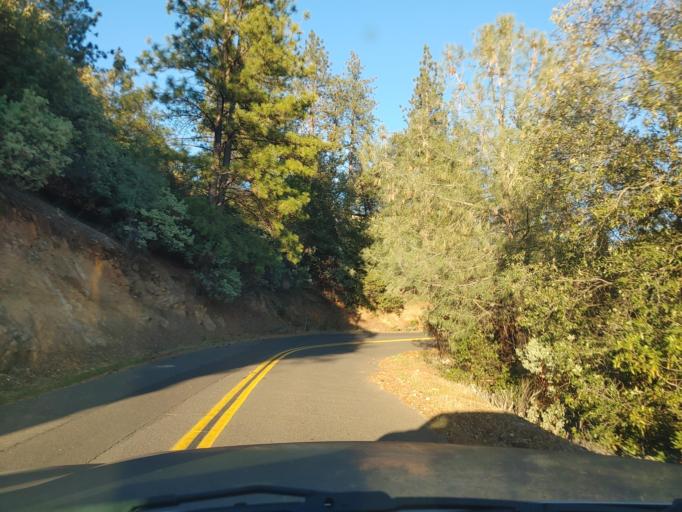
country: US
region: California
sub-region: Tuolumne County
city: Columbia
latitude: 38.0364
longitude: -120.3688
